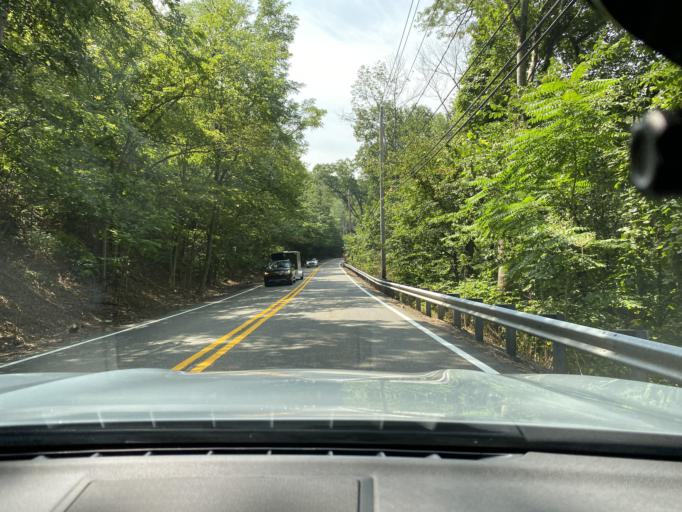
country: US
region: New Jersey
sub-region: Bergen County
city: Franklin Lakes
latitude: 41.0702
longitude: -74.2023
